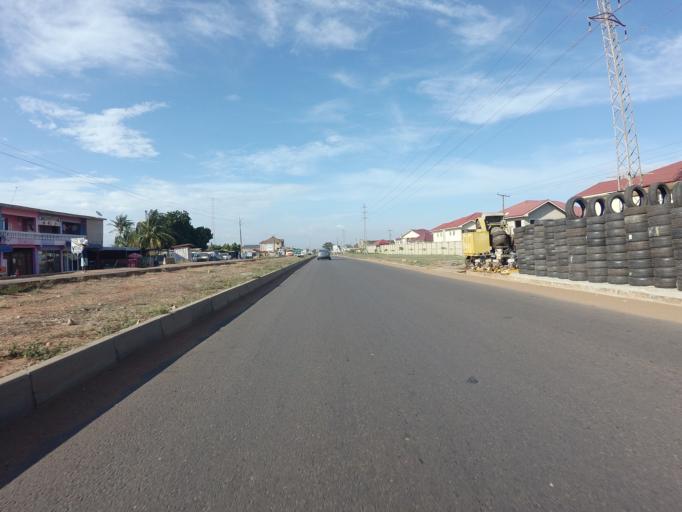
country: GH
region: Greater Accra
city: Nungua
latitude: 5.6355
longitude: -0.0637
